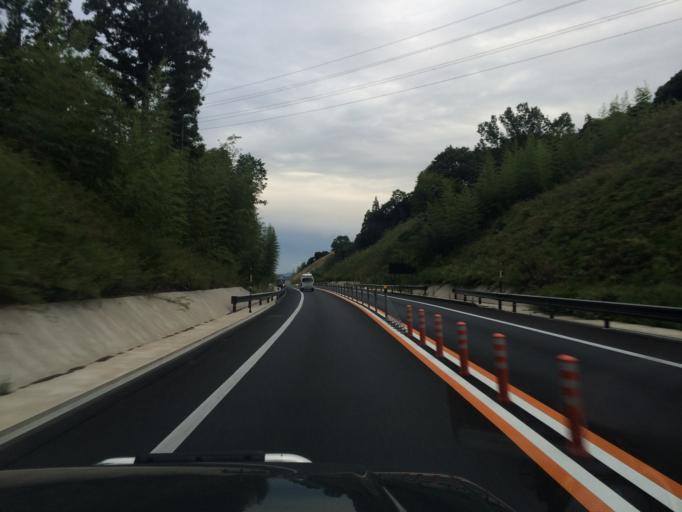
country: JP
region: Tottori
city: Tottori
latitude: 35.4951
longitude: 134.1793
